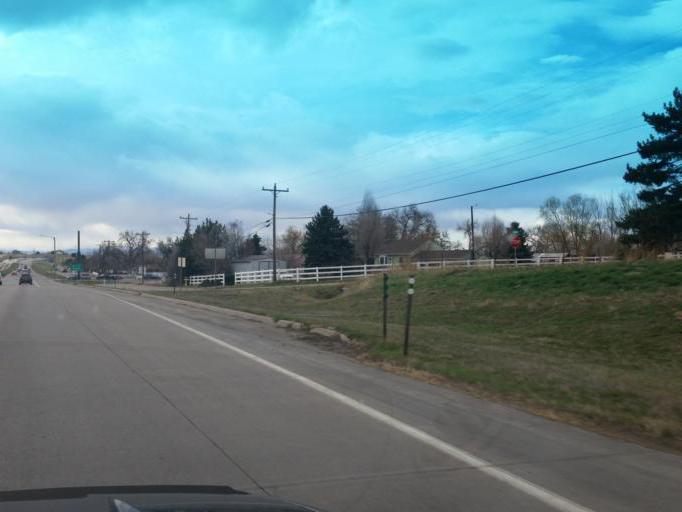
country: US
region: Colorado
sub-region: Weld County
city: Greeley
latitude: 40.3922
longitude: -104.7821
